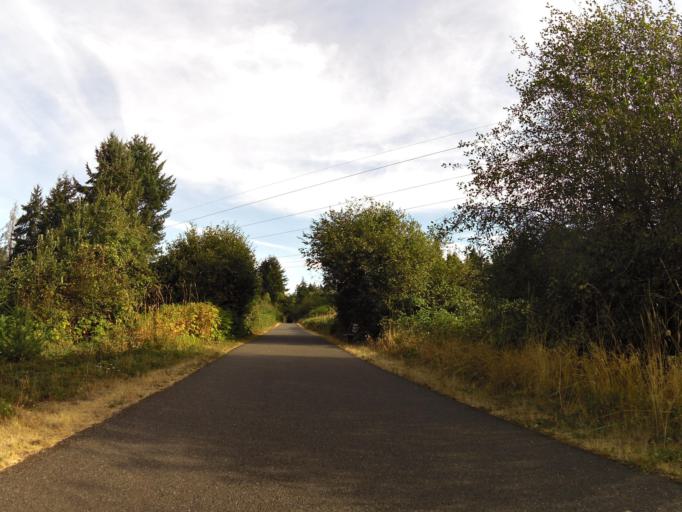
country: US
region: Washington
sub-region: Thurston County
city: Lacey
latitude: 46.9840
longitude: -122.8262
